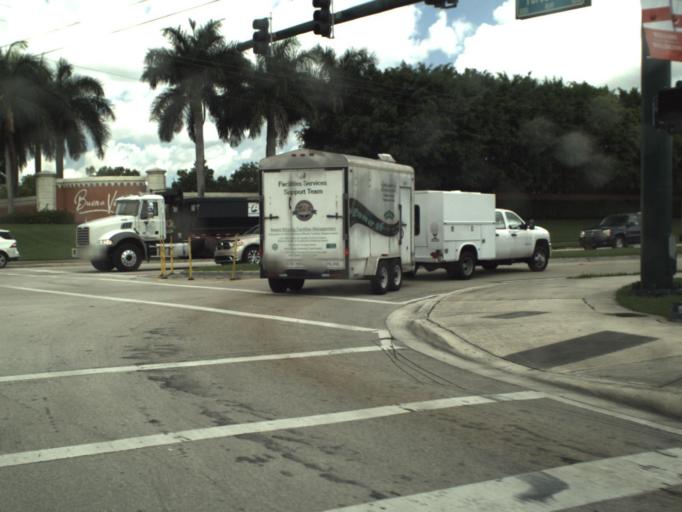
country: US
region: Florida
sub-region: Palm Beach County
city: Wellington
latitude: 26.6510
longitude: -80.1816
